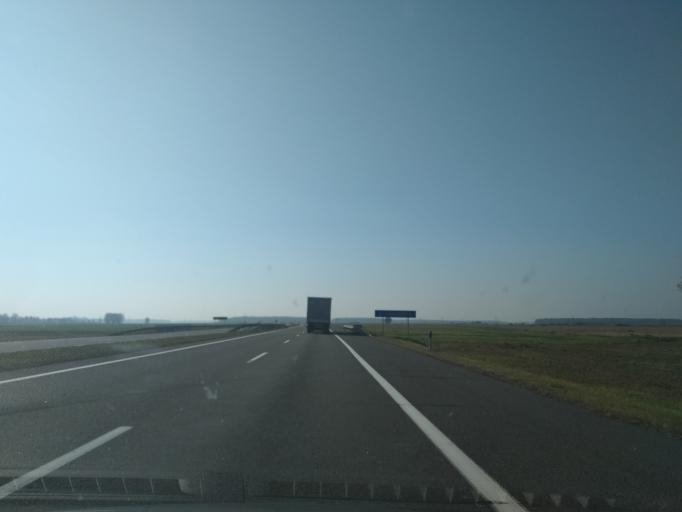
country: BY
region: Brest
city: Byaroza
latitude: 52.4302
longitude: 24.8428
